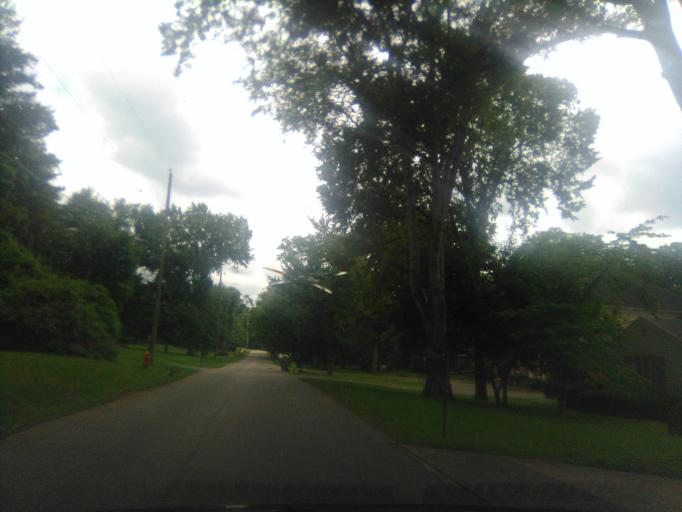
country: US
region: Tennessee
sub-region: Davidson County
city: Belle Meade
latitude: 36.0891
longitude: -86.8671
